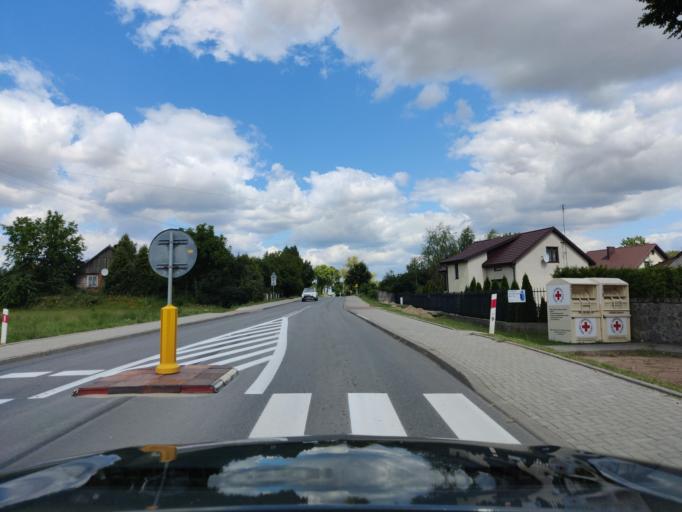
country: PL
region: Masovian Voivodeship
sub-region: Powiat wegrowski
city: Grebkow
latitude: 52.2704
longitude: 21.9121
